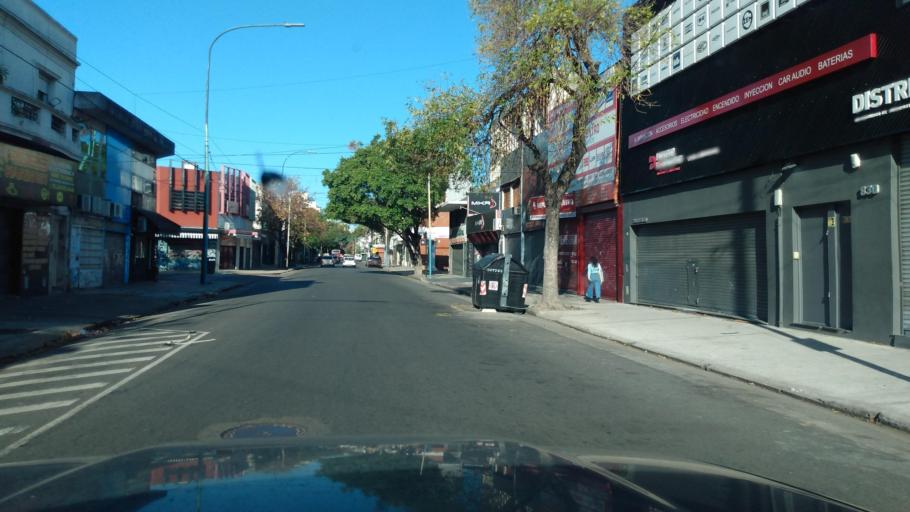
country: AR
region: Buenos Aires F.D.
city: Colegiales
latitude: -34.6003
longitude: -58.4480
